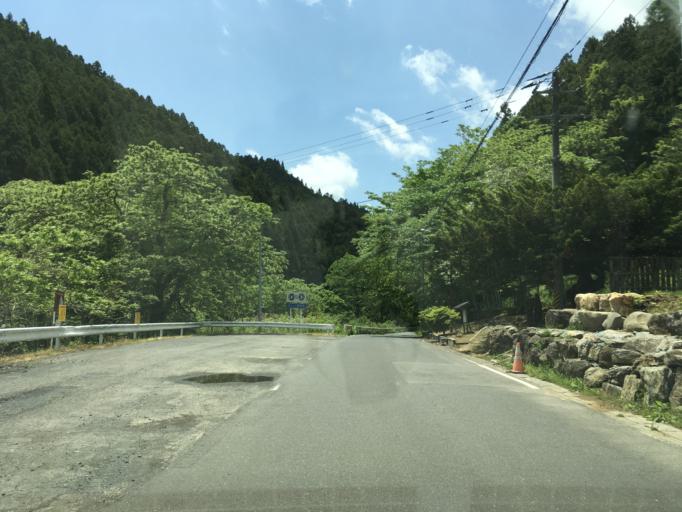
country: JP
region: Miyagi
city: Wakuya
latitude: 38.6711
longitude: 141.3418
